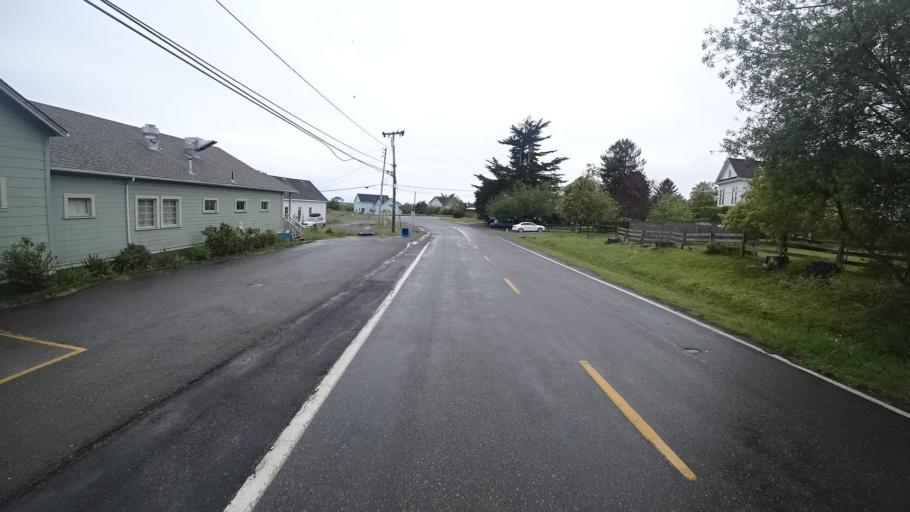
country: US
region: California
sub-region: Humboldt County
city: Bayside
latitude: 40.8421
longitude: -124.0629
